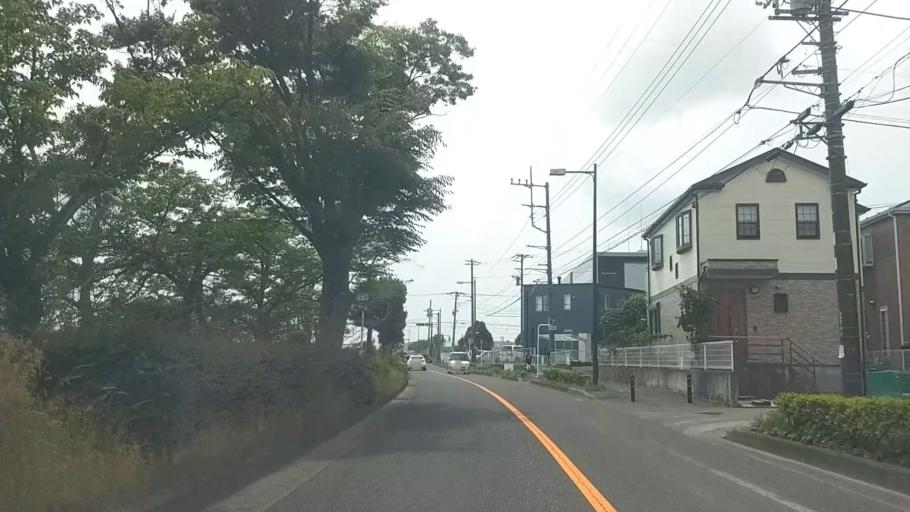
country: JP
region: Kanagawa
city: Fujisawa
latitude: 35.3432
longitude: 139.4664
